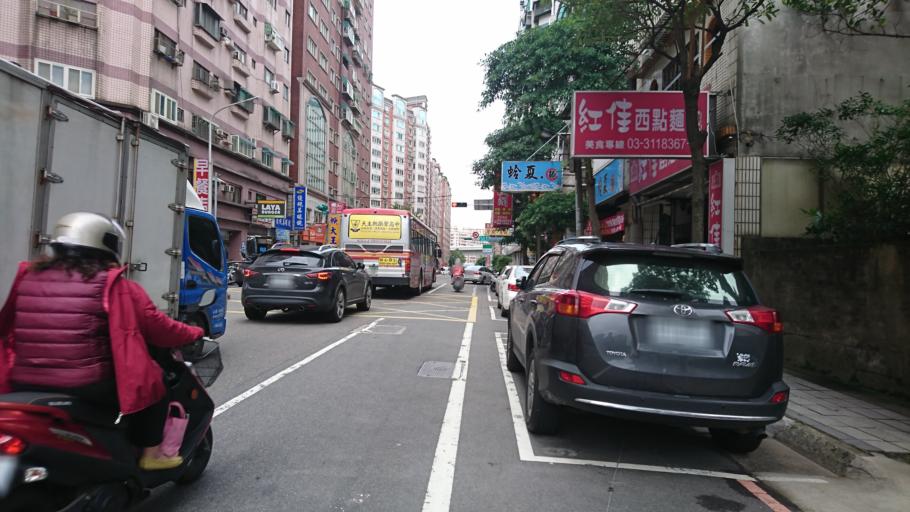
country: TW
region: Taiwan
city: Taoyuan City
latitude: 25.0554
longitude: 121.2986
